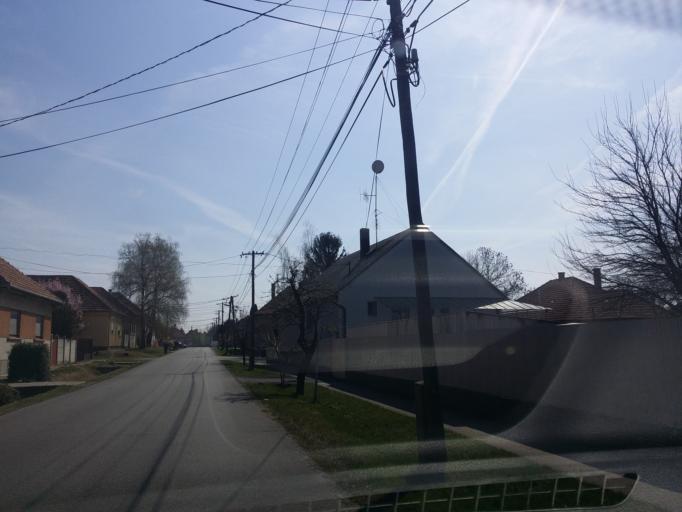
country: HU
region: Pest
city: Cegledbercel
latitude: 47.2179
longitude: 19.6780
